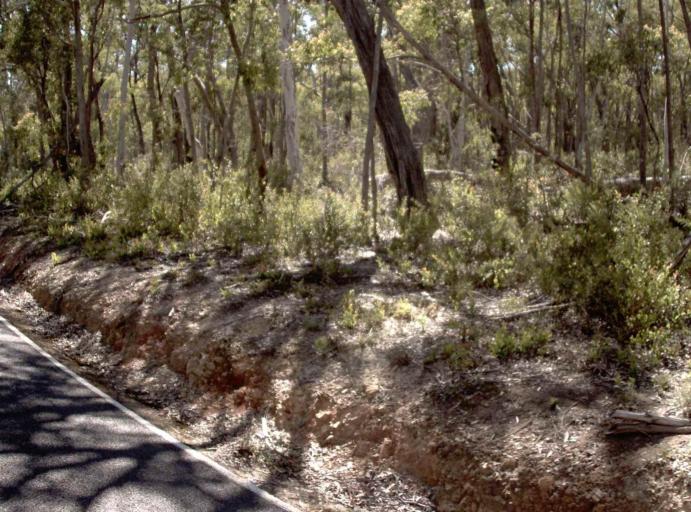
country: AU
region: New South Wales
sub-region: Bombala
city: Bombala
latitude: -37.1393
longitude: 148.7323
